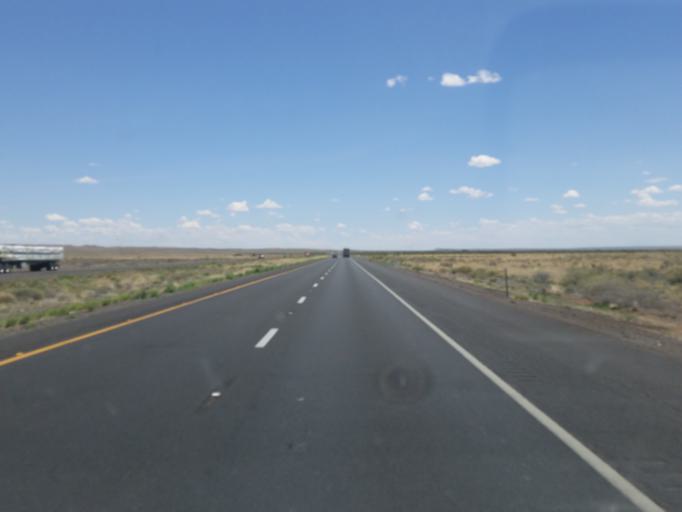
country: US
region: Arizona
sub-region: Navajo County
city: Winslow
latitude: 34.9985
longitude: -110.5942
